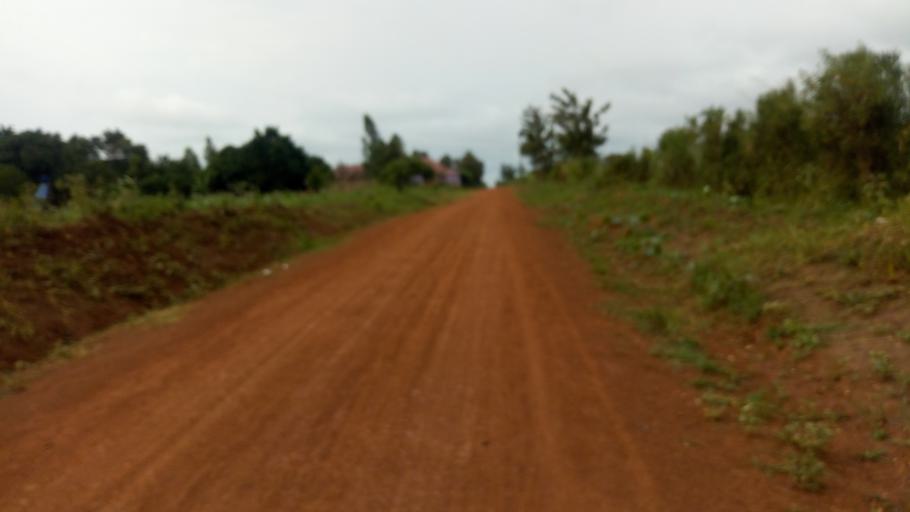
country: UG
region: Western Region
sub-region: Kiryandongo District
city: Kiryandongo
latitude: 1.8050
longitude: 32.0140
